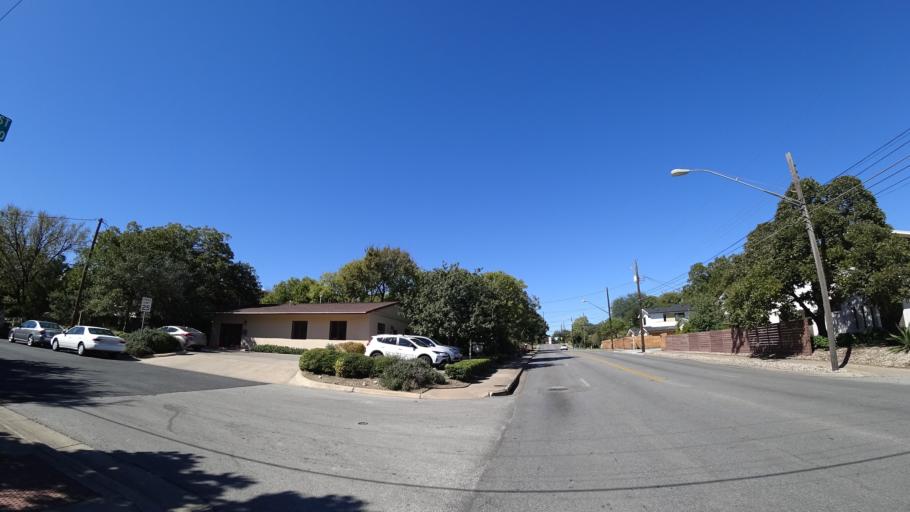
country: US
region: Texas
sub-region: Travis County
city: Austin
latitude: 30.2427
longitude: -97.7613
